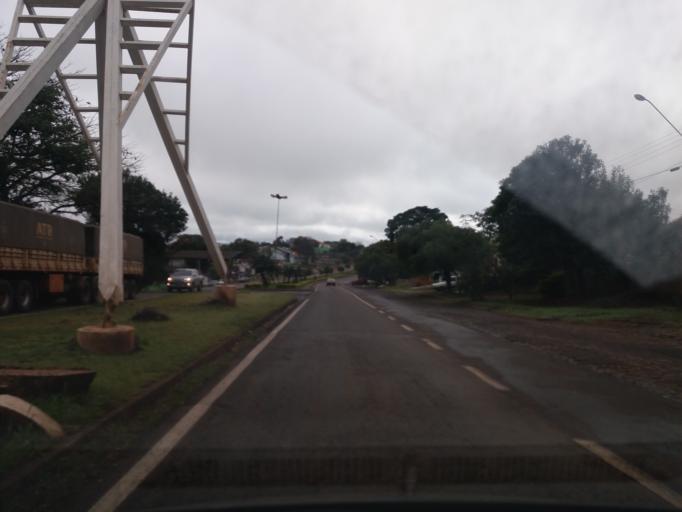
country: BR
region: Parana
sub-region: Cascavel
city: Cascavel
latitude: -25.2838
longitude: -53.5686
